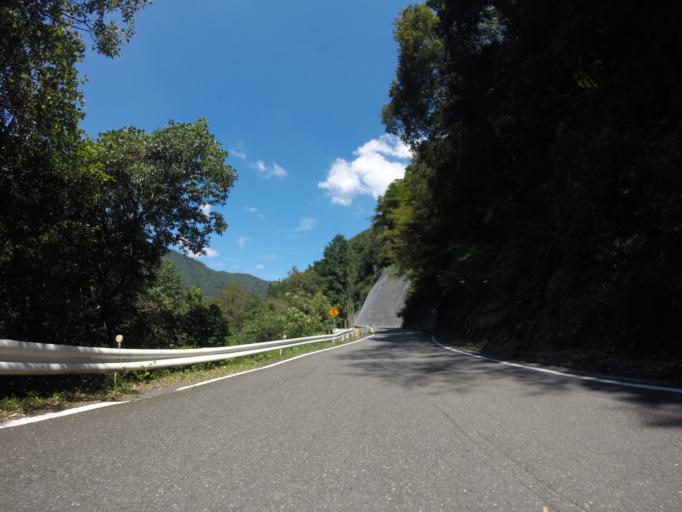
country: JP
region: Shizuoka
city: Shizuoka-shi
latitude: 35.0496
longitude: 138.2404
